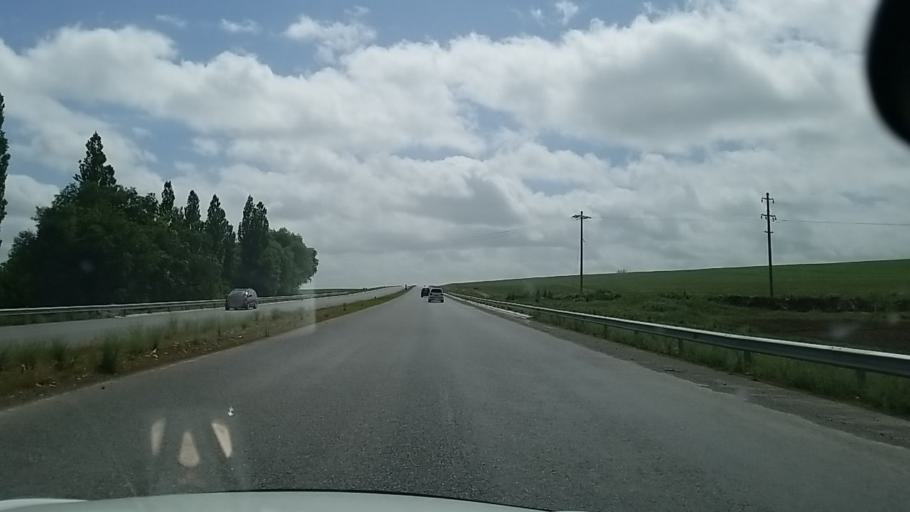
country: KZ
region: Ongtustik Qazaqstan
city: Kokterek
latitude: 42.5475
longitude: 70.1719
